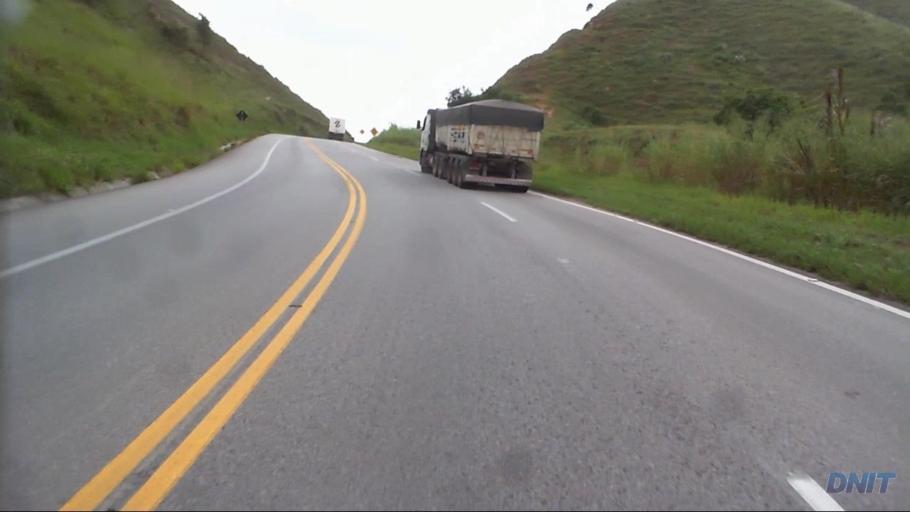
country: BR
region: Minas Gerais
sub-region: Nova Era
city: Nova Era
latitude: -19.6696
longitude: -42.9701
